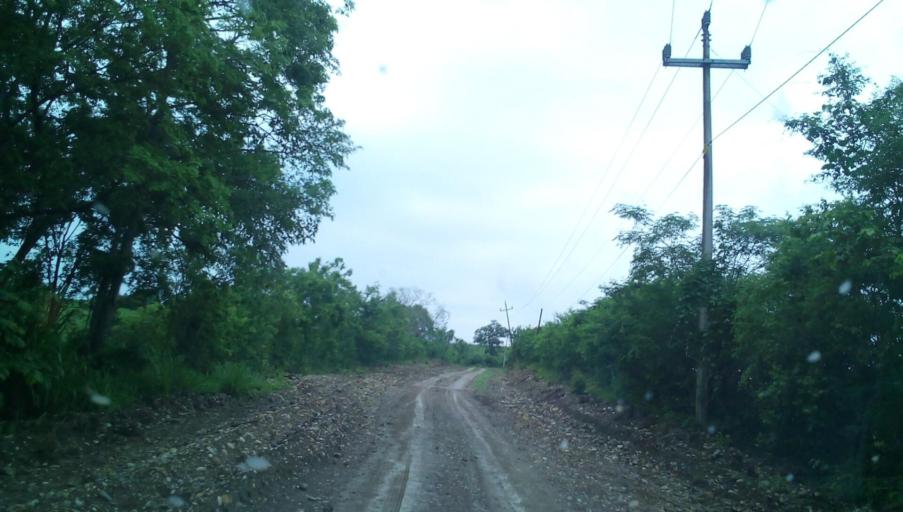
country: MX
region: Veracruz
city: Tempoal de Sanchez
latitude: 21.4510
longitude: -98.4254
